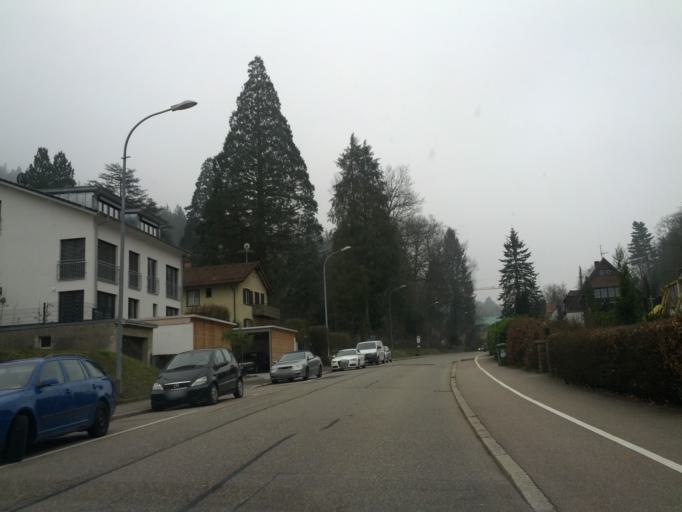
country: DE
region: Baden-Wuerttemberg
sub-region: Freiburg Region
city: Horben
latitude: 47.9606
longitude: 7.8632
